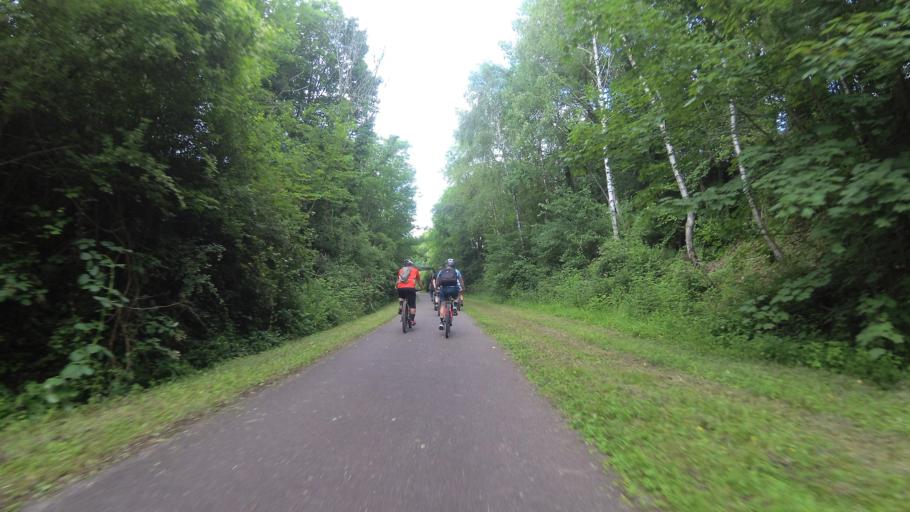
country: FR
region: Lorraine
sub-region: Departement de la Moselle
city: Bliesbruck
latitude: 49.1153
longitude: 7.1837
